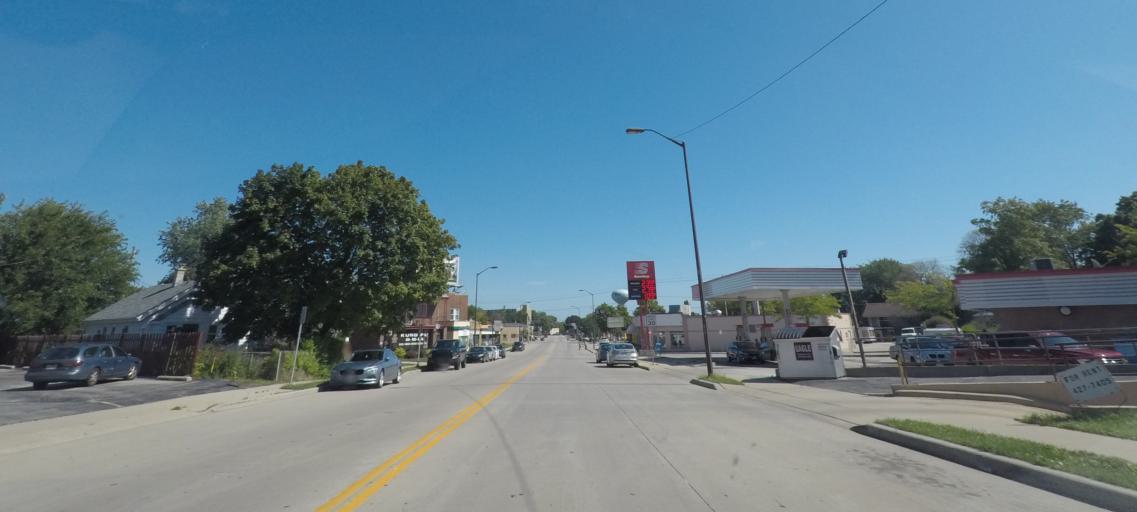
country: US
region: Wisconsin
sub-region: Milwaukee County
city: West Allis
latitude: 43.0051
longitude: -88.0268
